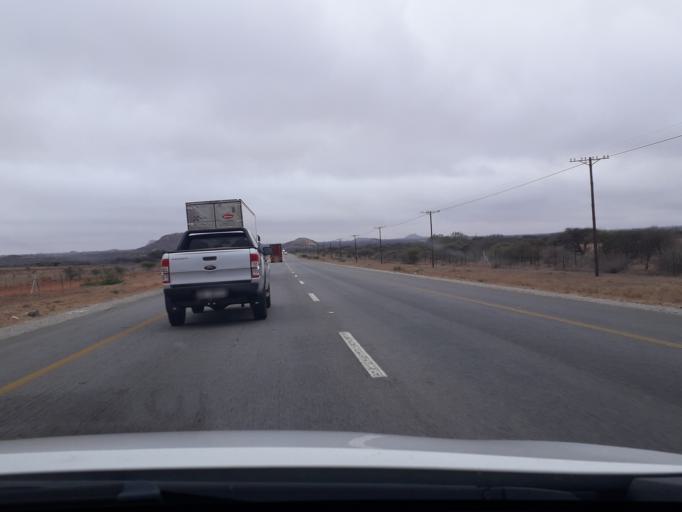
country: ZA
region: Limpopo
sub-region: Capricorn District Municipality
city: Mankoeng
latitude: -23.5543
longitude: 29.6876
